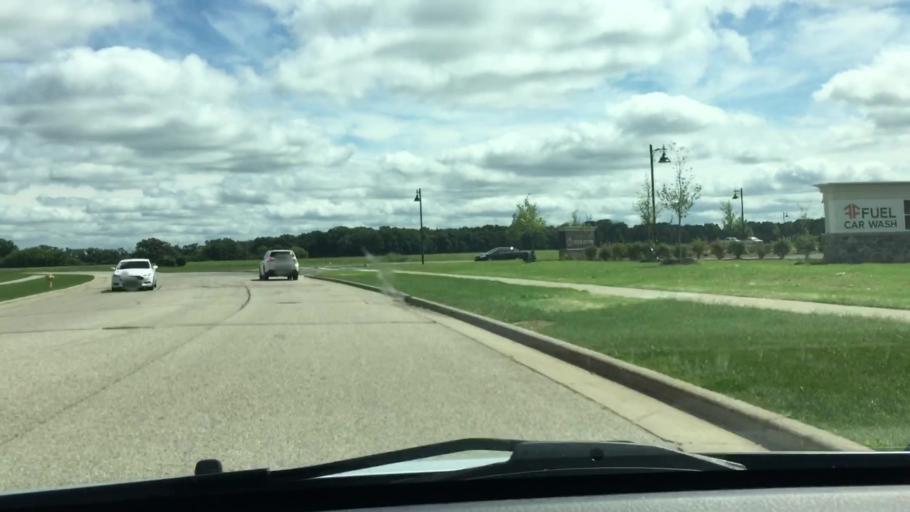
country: US
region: Wisconsin
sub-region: Waukesha County
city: Oconomowoc
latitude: 43.0721
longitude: -88.4661
